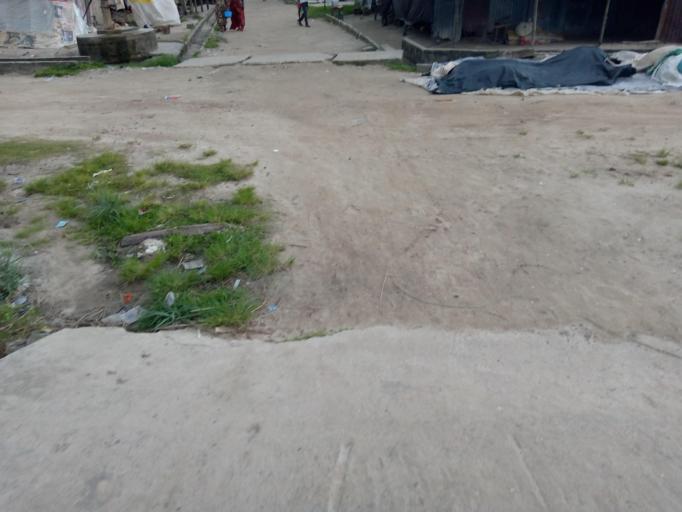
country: SL
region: Southern Province
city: Bonthe
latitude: 7.5287
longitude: -12.5030
